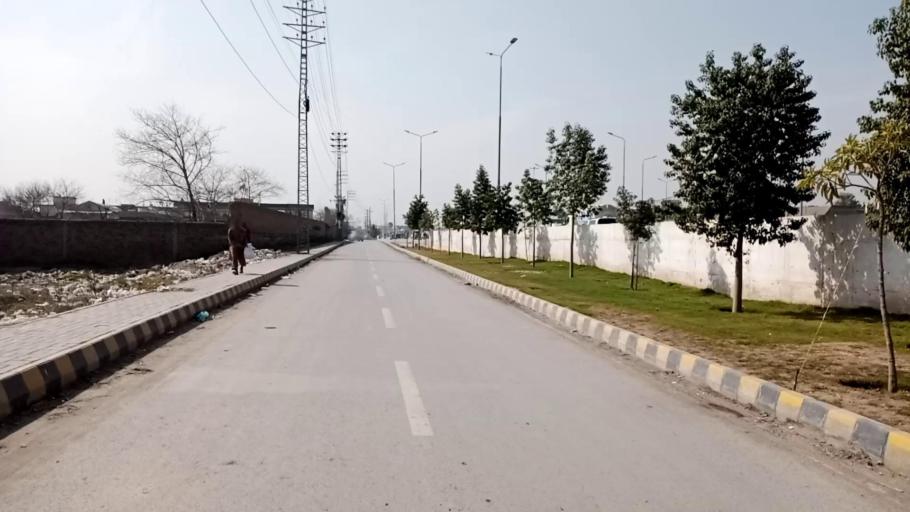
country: PK
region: Khyber Pakhtunkhwa
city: Peshawar
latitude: 34.0181
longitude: 71.6354
